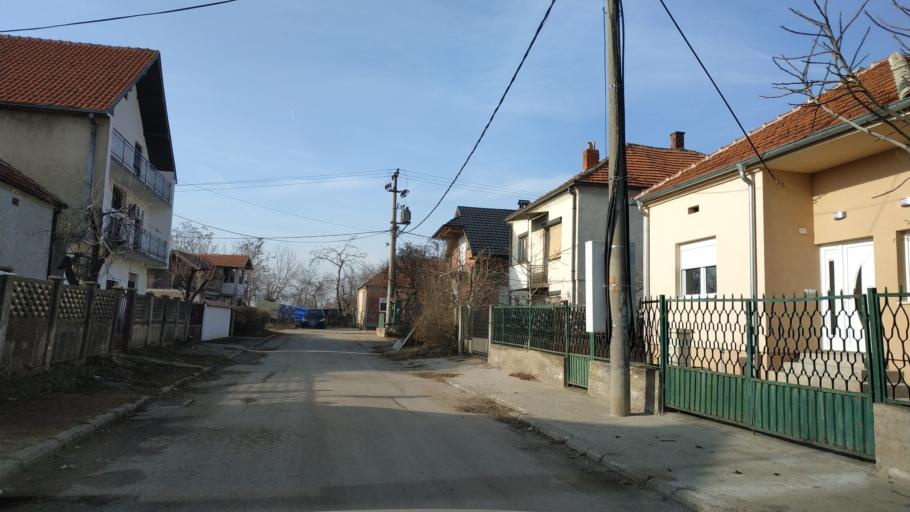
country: RS
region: Central Serbia
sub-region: Nisavski Okrug
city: Aleksinac
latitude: 43.5382
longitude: 21.6971
